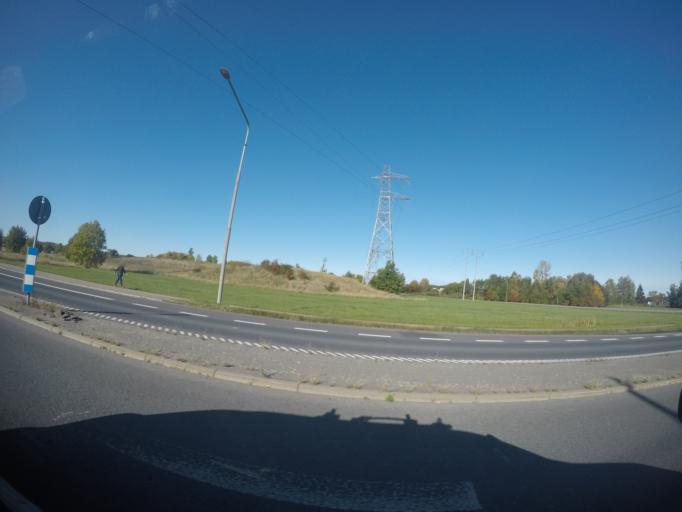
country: SE
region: Vaestmanland
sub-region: Vasteras
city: Vasteras
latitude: 59.5904
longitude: 16.4691
